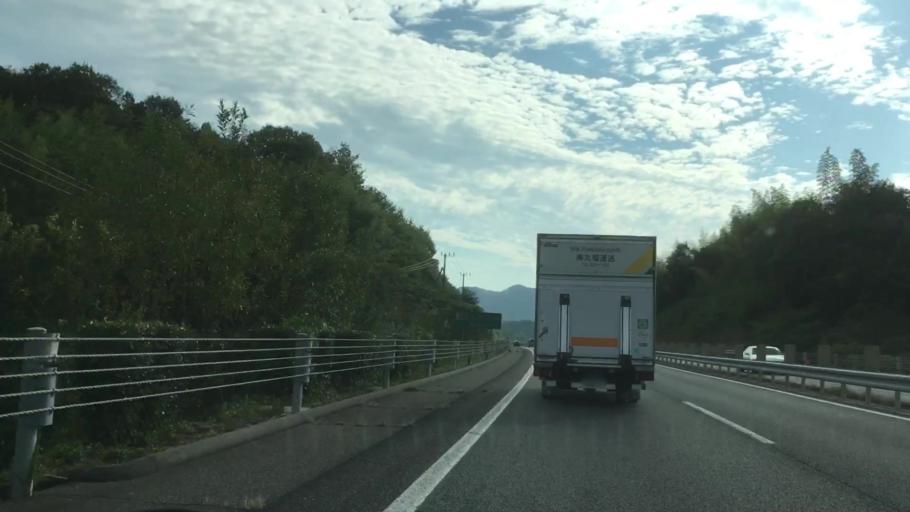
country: JP
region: Yamaguchi
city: Yanai
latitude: 34.0960
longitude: 132.0981
